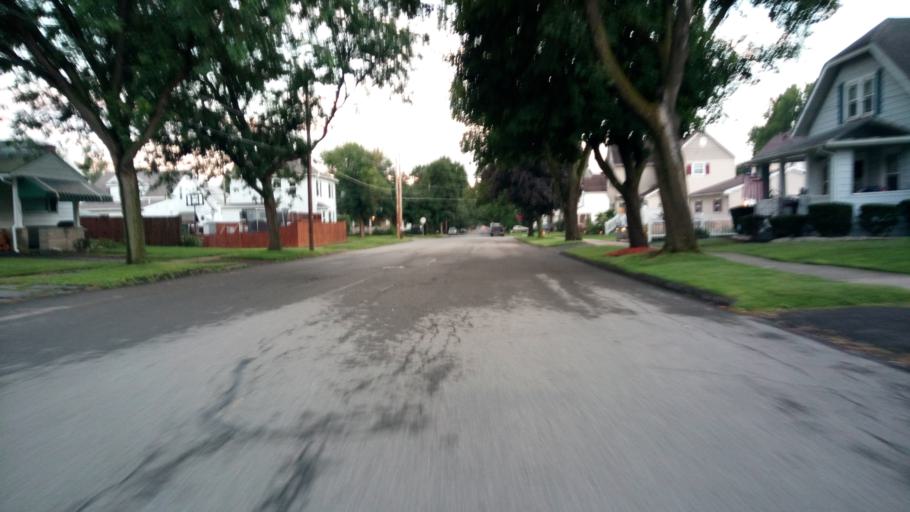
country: US
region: New York
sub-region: Chemung County
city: Elmira
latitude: 42.0965
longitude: -76.8253
